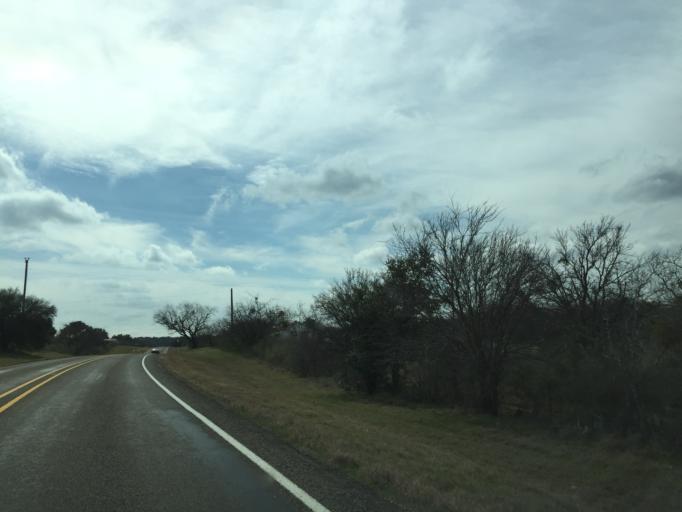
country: US
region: Texas
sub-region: Burnet County
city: Granite Shoals
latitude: 30.5301
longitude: -98.4457
